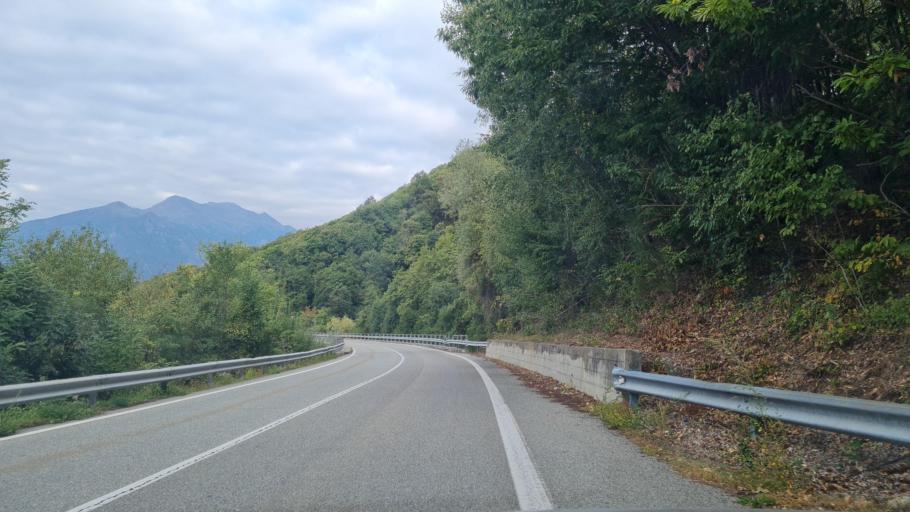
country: IT
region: Piedmont
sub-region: Provincia di Biella
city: Donato
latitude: 45.5154
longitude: 7.8989
